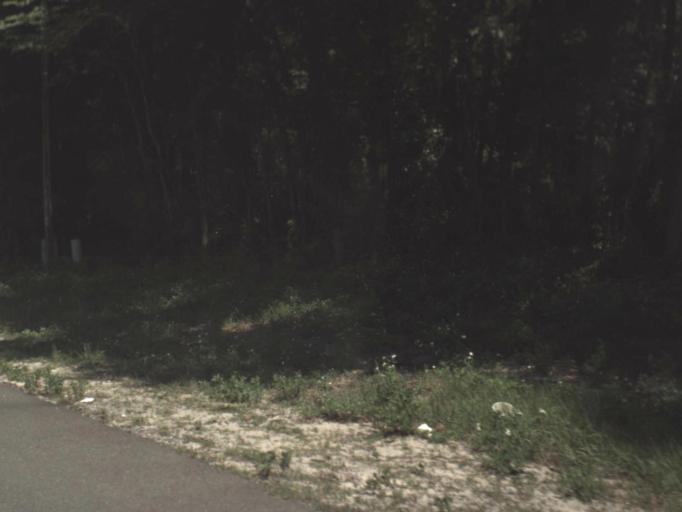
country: US
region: Florida
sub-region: Clay County
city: Keystone Heights
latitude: 29.8000
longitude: -82.0545
